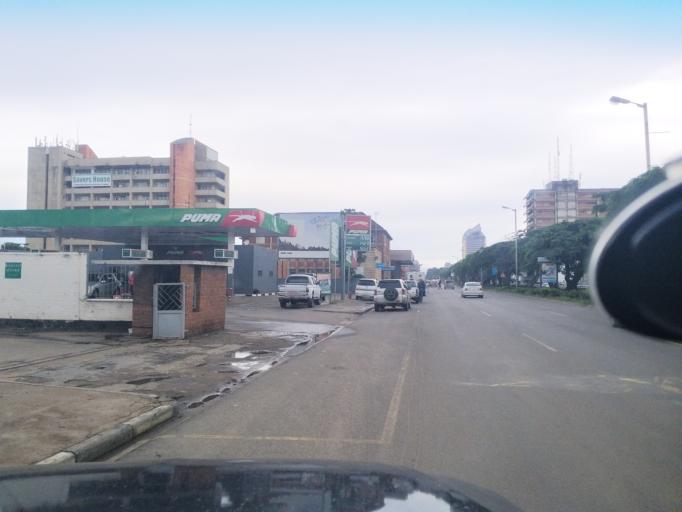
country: ZM
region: Lusaka
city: Lusaka
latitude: -15.4105
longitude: 28.2808
